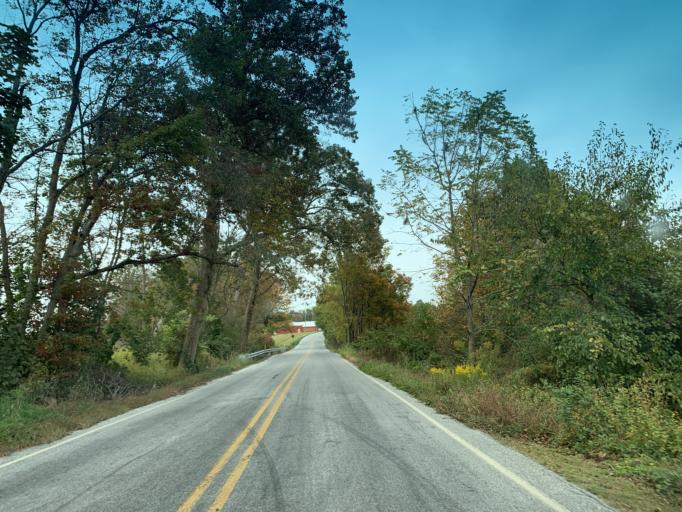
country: US
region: Pennsylvania
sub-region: York County
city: Windsor
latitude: 39.8521
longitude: -76.5128
